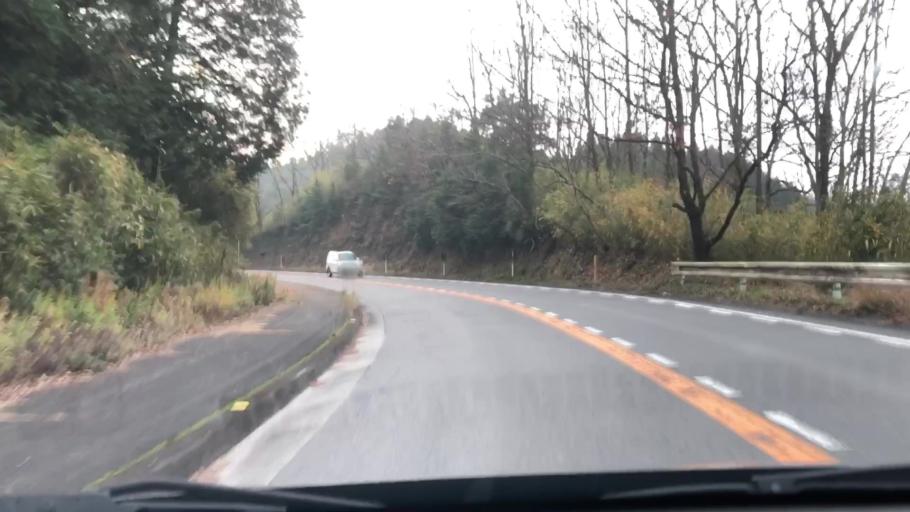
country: JP
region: Oita
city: Takedamachi
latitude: 32.9700
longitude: 131.5054
